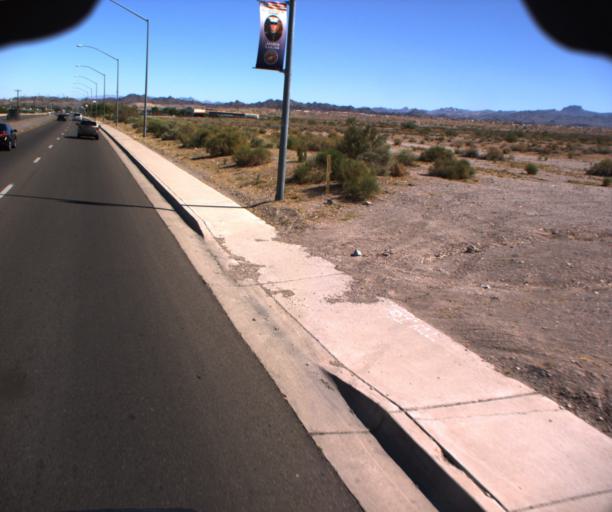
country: US
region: Arizona
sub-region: Mohave County
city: Bullhead City
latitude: 35.1576
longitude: -114.5668
